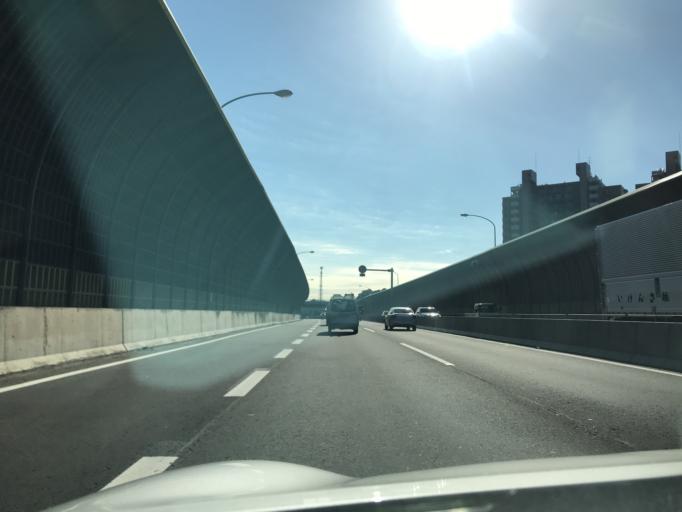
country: JP
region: Chiba
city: Chiba
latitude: 35.6311
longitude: 140.1277
